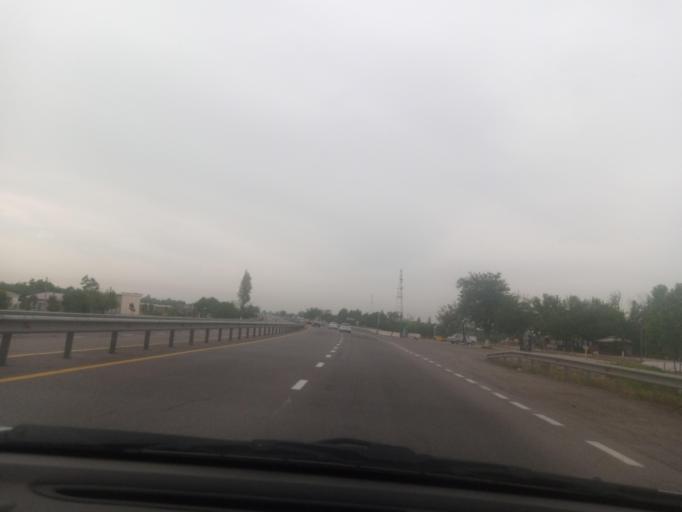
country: UZ
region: Toshkent
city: Tuytepa
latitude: 41.1272
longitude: 69.4374
